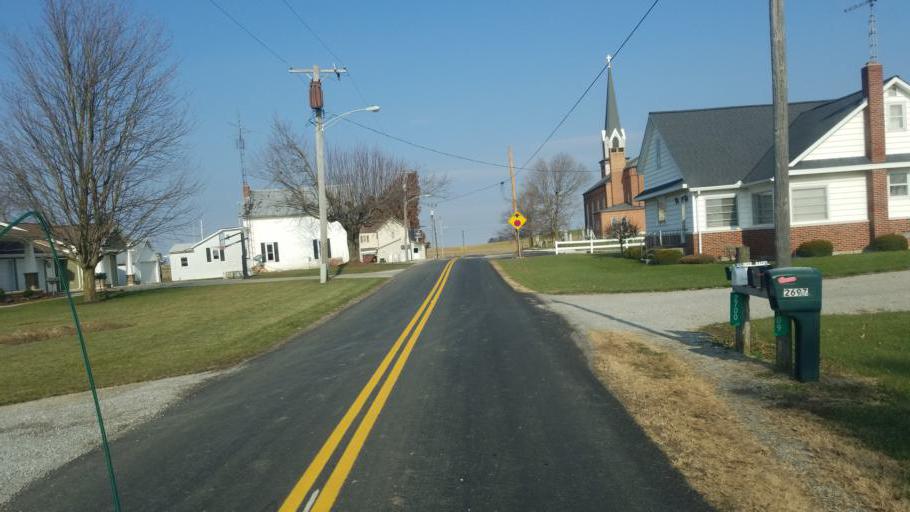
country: US
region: Ohio
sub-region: Mercer County
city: Fort Recovery
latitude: 40.4270
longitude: -84.7390
